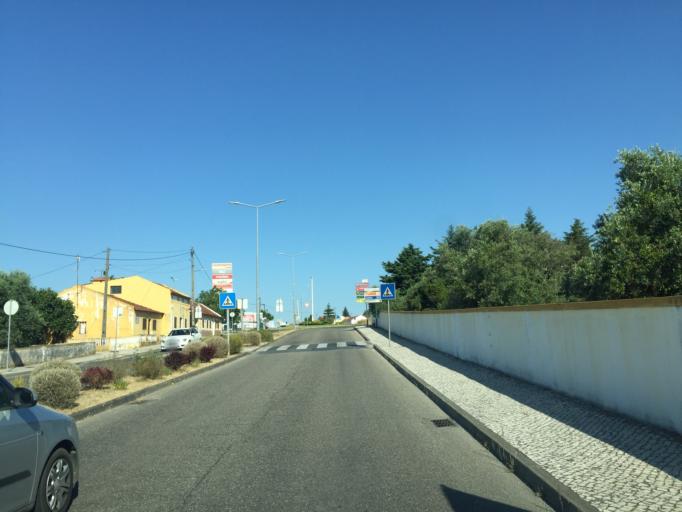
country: PT
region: Santarem
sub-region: Tomar
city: Tomar
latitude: 39.6018
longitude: -8.3941
